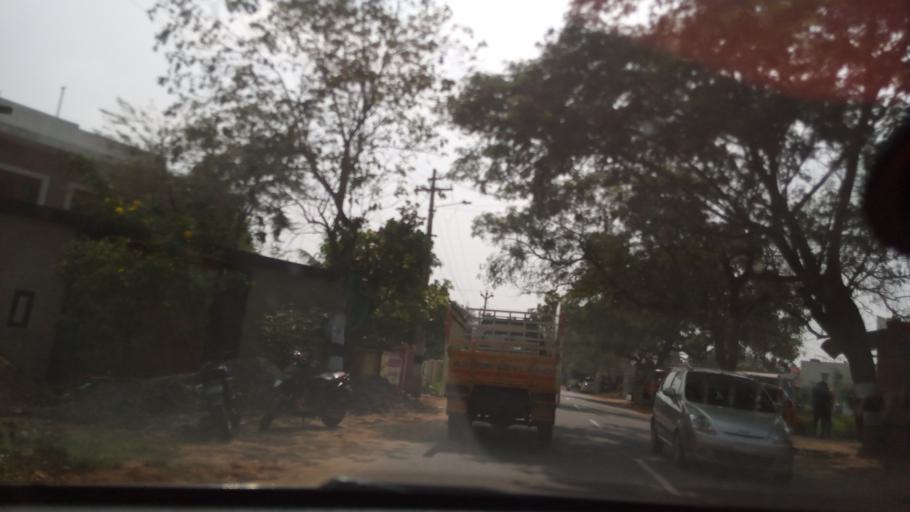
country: IN
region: Tamil Nadu
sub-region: Coimbatore
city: Perur
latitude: 11.0047
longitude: 76.8618
